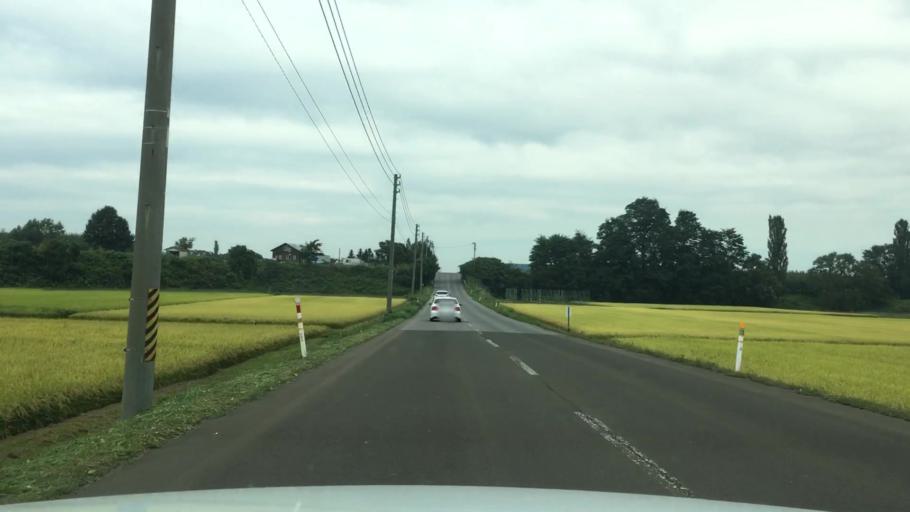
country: JP
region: Aomori
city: Hirosaki
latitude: 40.6511
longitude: 140.4222
